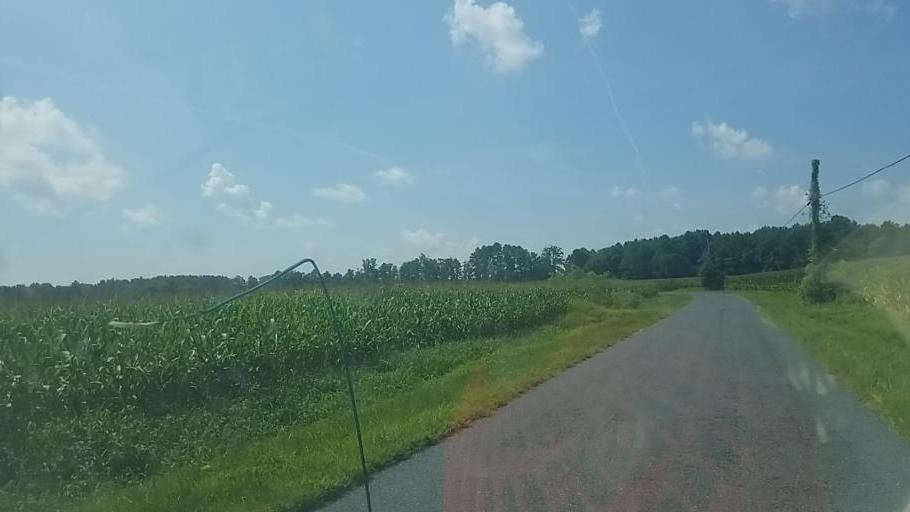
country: US
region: Maryland
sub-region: Worcester County
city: Berlin
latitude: 38.2928
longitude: -75.2952
